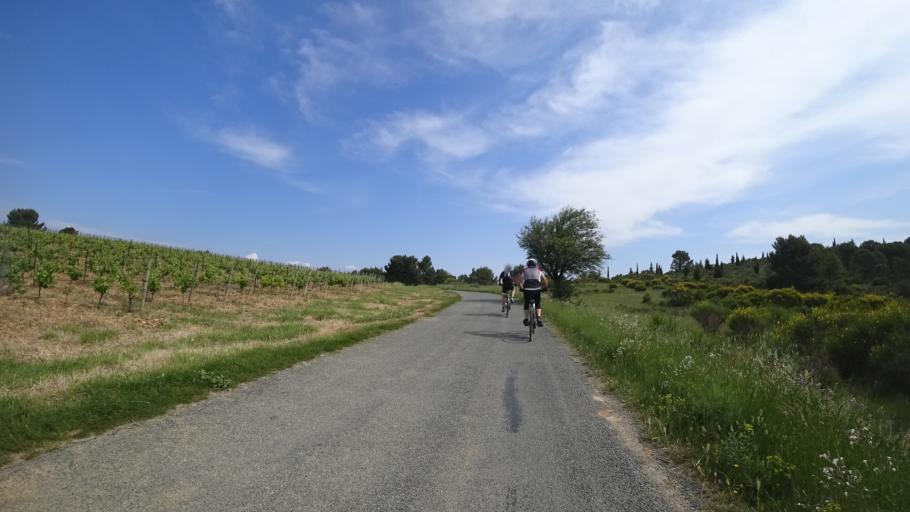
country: FR
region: Languedoc-Roussillon
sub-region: Departement de l'Aude
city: Canet
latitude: 43.2583
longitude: 2.8057
